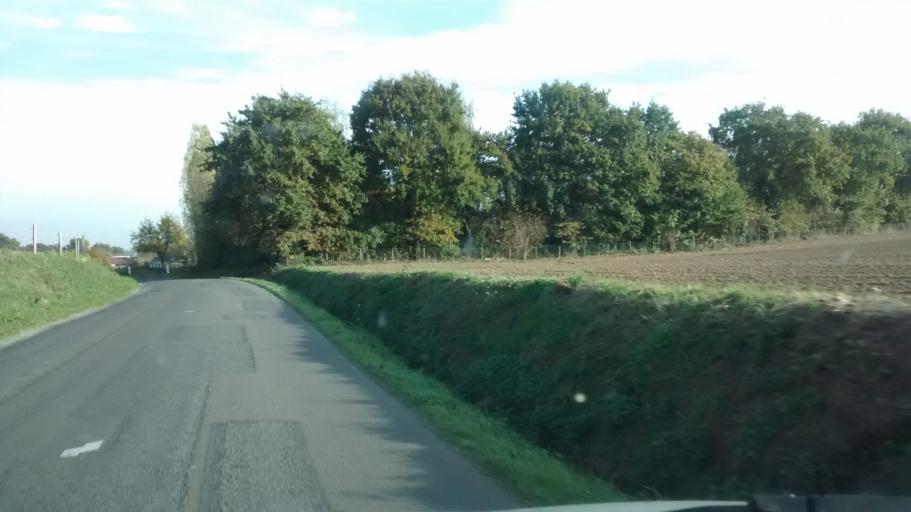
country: FR
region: Brittany
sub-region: Departement d'Ille-et-Vilaine
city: Betton
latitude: 48.1891
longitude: -1.6599
